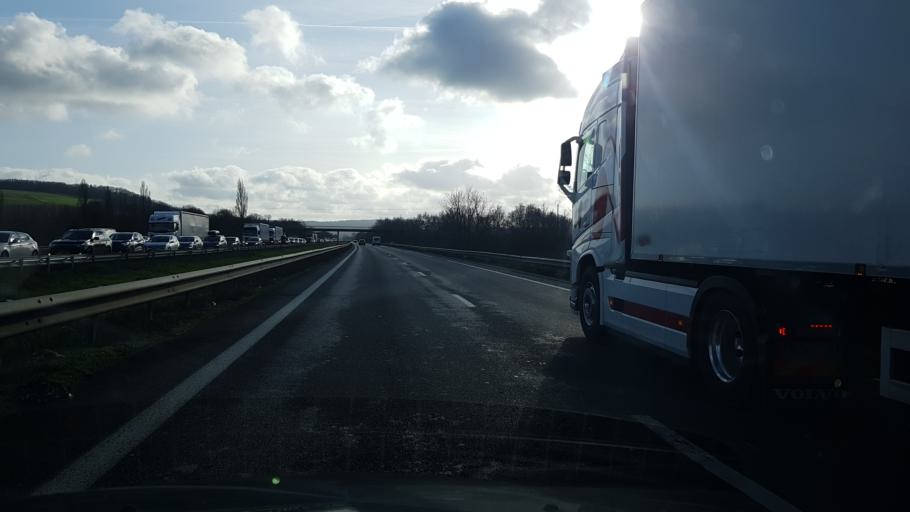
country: FR
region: Lorraine
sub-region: Departement de Meurthe-et-Moselle
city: Dieulouard
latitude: 48.8511
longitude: 6.0891
